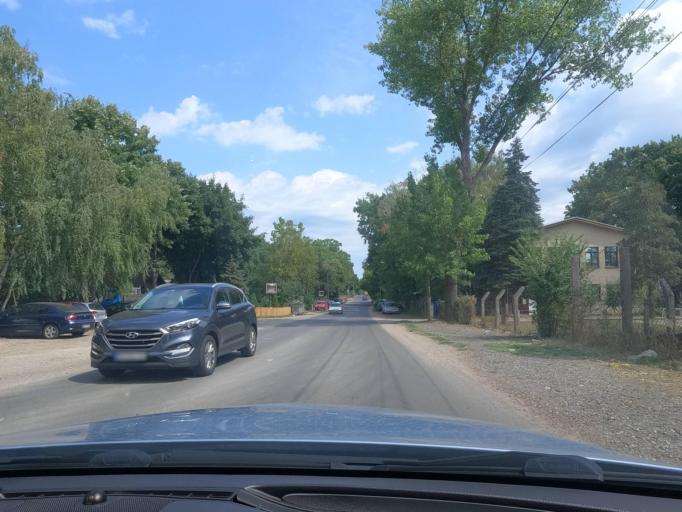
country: RS
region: Central Serbia
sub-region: Belgrade
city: Zemun
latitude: 44.8240
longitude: 20.3808
